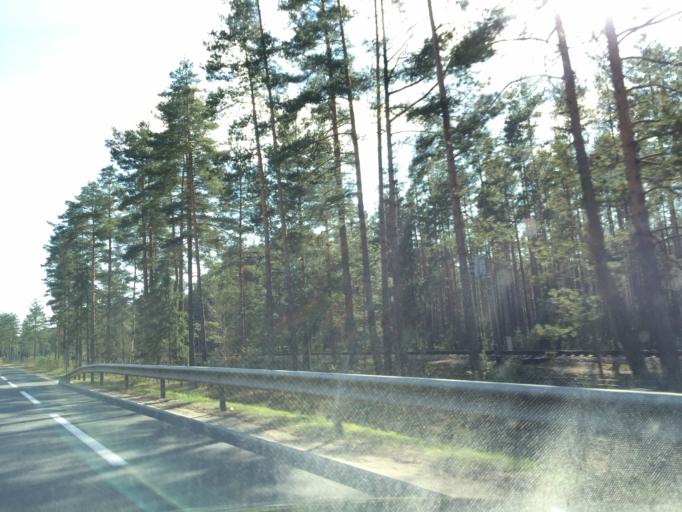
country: LV
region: Saulkrastu
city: Saulkrasti
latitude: 57.2887
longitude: 24.4346
